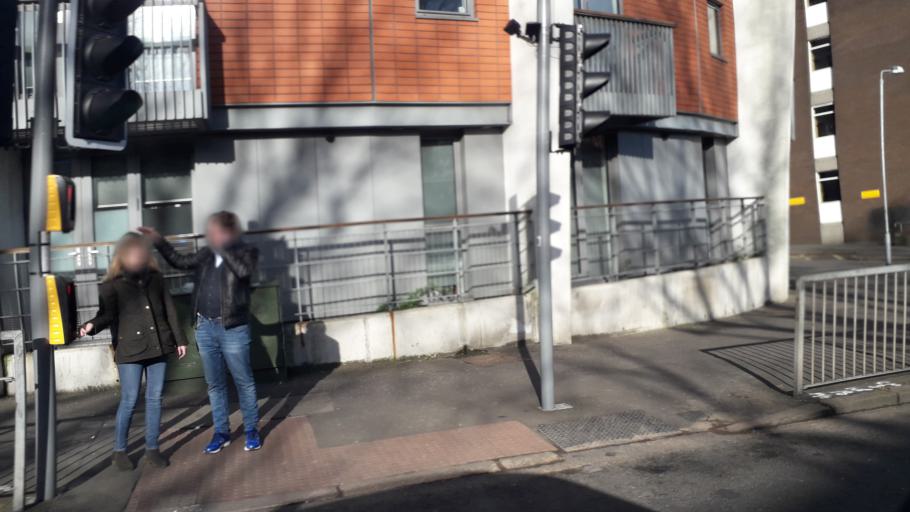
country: GB
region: Northern Ireland
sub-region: City of Belfast
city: Belfast
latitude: 54.5846
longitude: -5.9423
